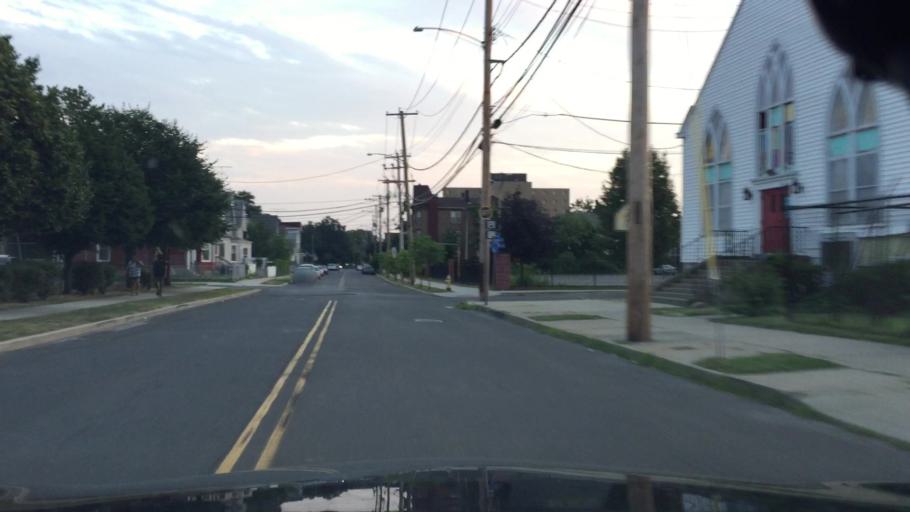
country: US
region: Connecticut
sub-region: Fairfield County
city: Bridgeport
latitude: 41.1694
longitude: -73.1876
